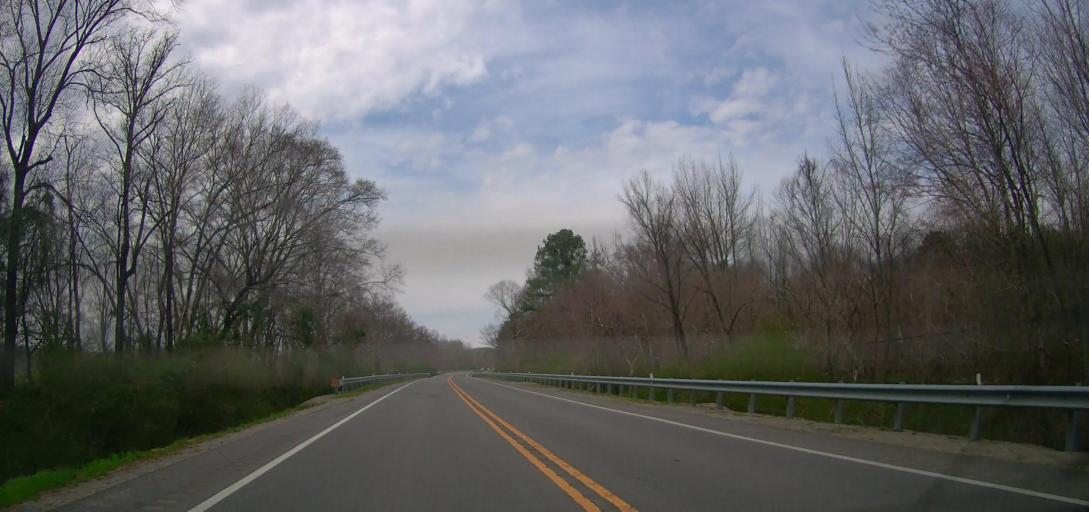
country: US
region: Alabama
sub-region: Marion County
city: Guin
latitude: 33.9947
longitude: -87.9290
